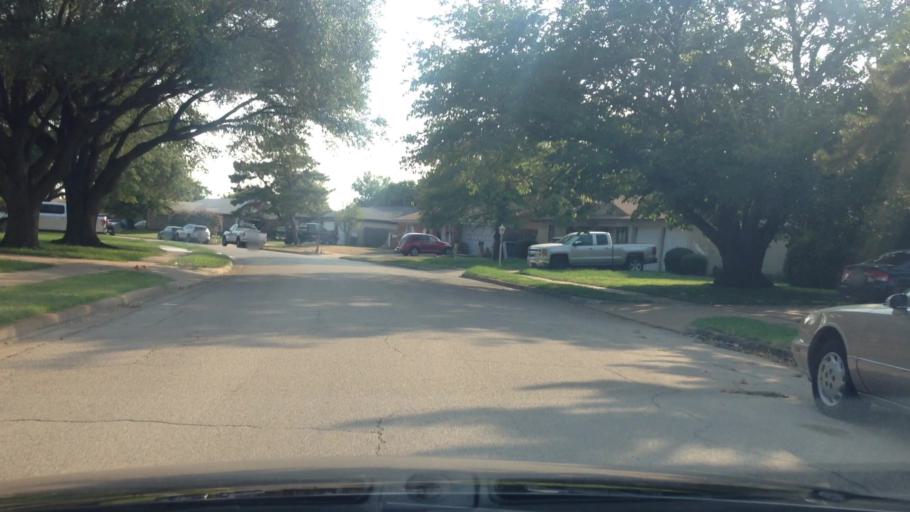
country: US
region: Texas
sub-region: Tarrant County
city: Edgecliff Village
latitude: 32.6512
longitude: -97.3453
